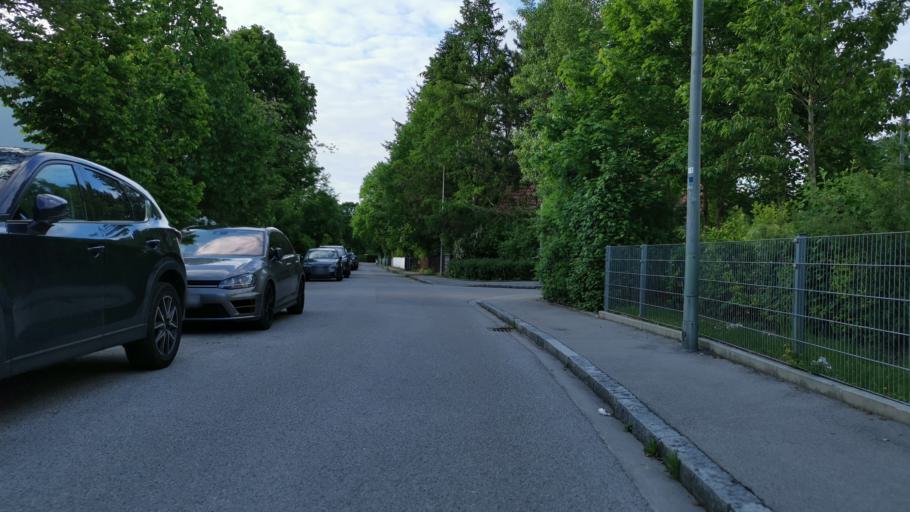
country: DE
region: Bavaria
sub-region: Upper Bavaria
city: Neuried
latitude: 48.0770
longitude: 11.4923
